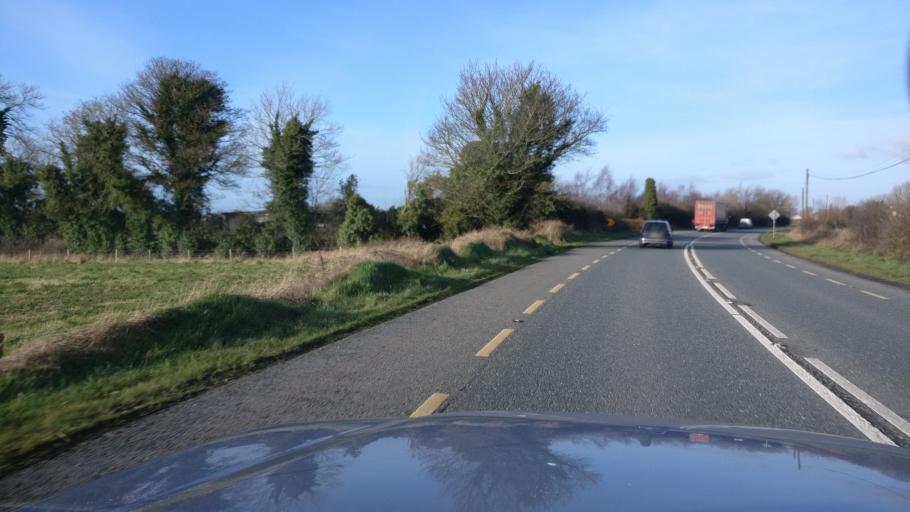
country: IE
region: Leinster
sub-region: Uibh Fhaili
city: Tullamore
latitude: 53.2365
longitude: -7.4784
